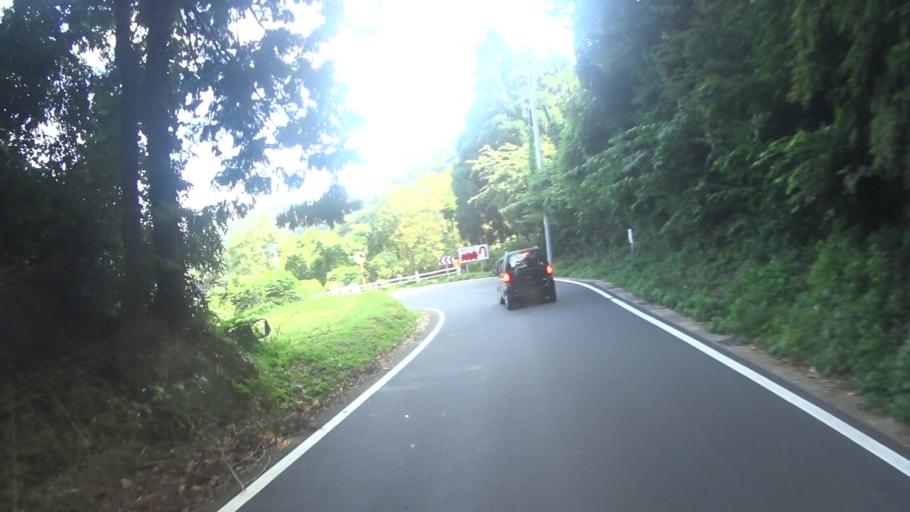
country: JP
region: Kyoto
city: Miyazu
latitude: 35.7480
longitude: 135.2515
